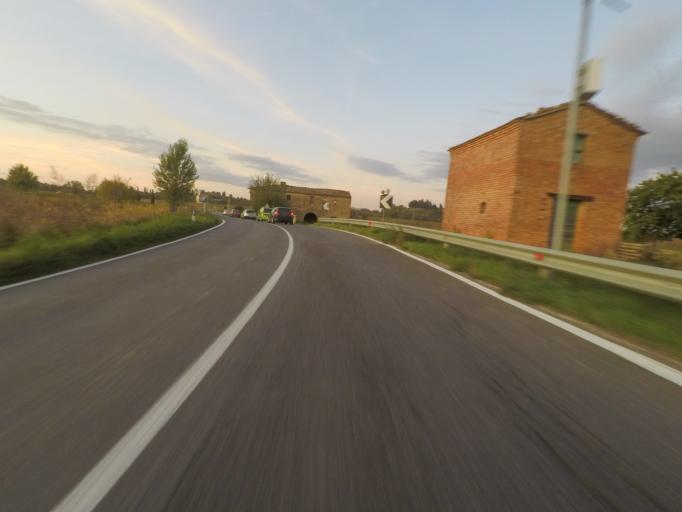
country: IT
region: Tuscany
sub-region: Provincia di Siena
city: Guazzino
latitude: 43.2034
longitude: 11.7659
